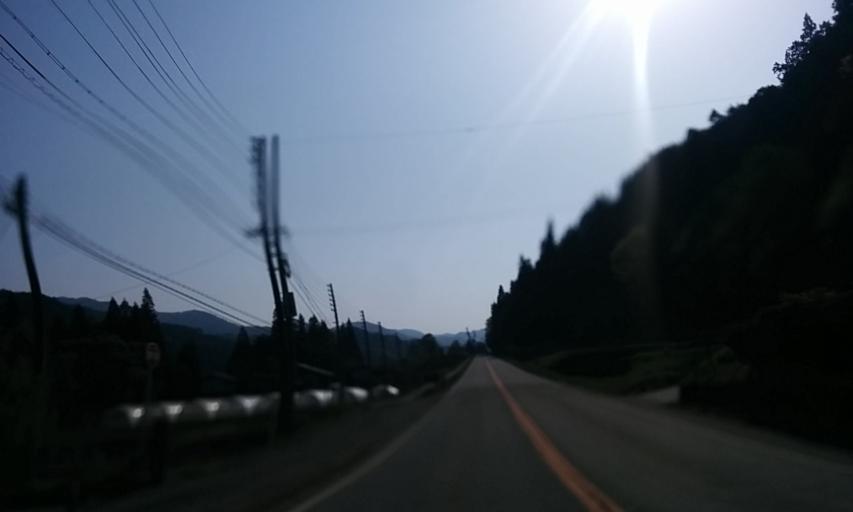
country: JP
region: Gifu
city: Takayama
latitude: 36.1724
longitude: 137.3539
